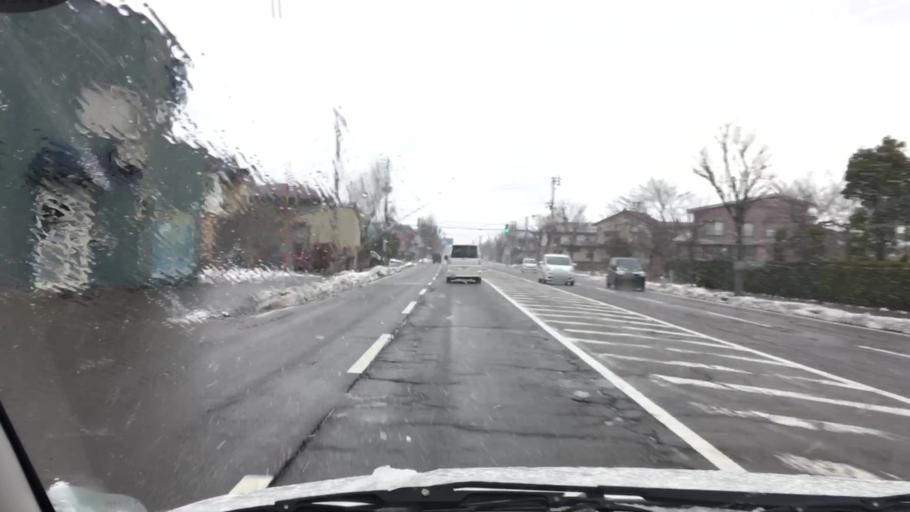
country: JP
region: Niigata
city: Joetsu
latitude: 37.1193
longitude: 138.2327
